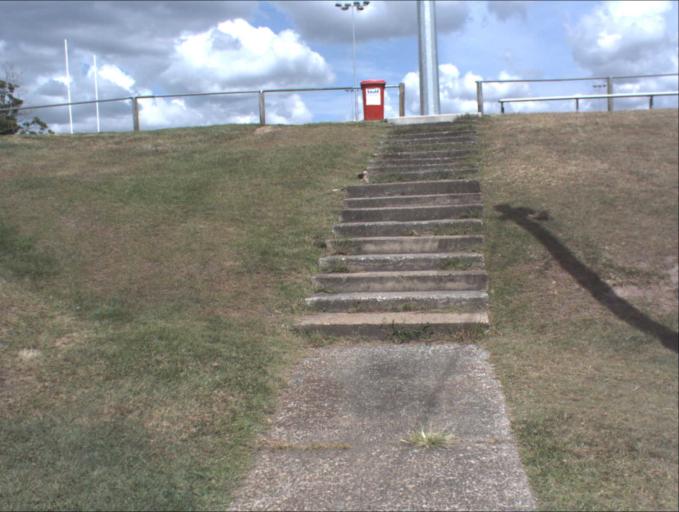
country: AU
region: Queensland
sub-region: Logan
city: Beenleigh
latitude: -27.7189
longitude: 153.1965
